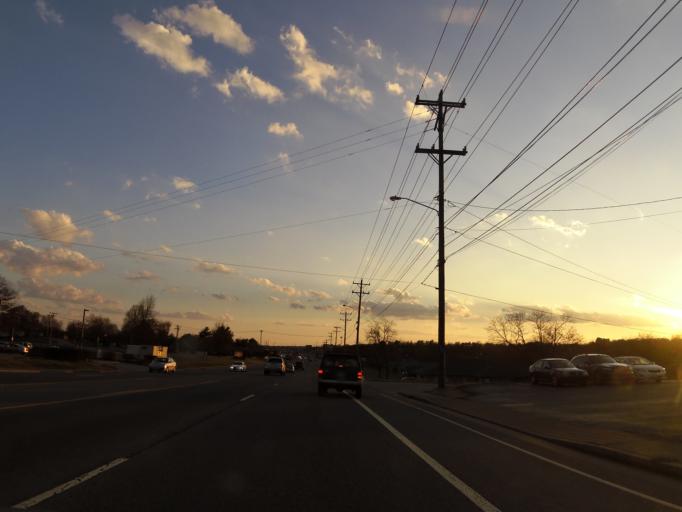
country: US
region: Tennessee
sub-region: Davidson County
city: Lakewood
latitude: 36.2063
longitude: -86.6133
